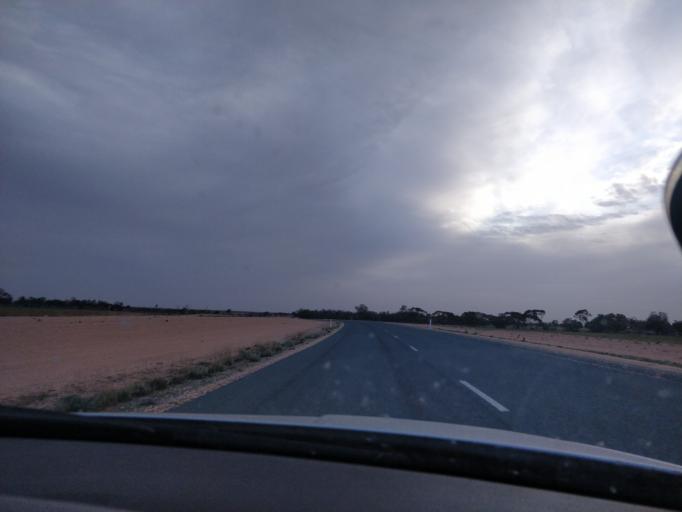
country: AU
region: New South Wales
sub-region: Wentworth
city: Gol Gol
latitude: -34.0358
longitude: 142.3590
